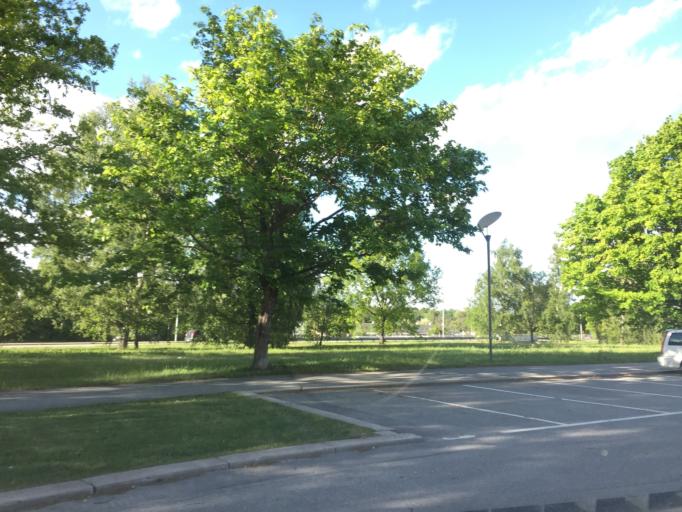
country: SE
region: OErebro
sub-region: Orebro Kommun
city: Orebro
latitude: 59.2759
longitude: 15.1628
